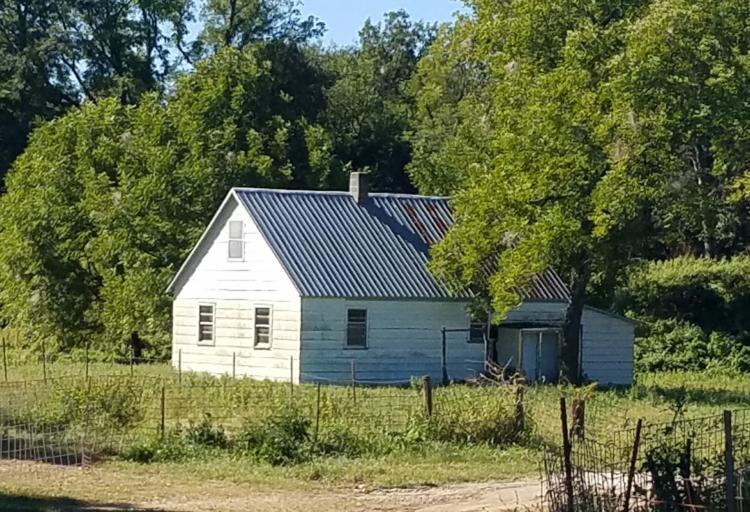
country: US
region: Missouri
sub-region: Cooper County
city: Boonville
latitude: 38.8520
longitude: -92.6595
